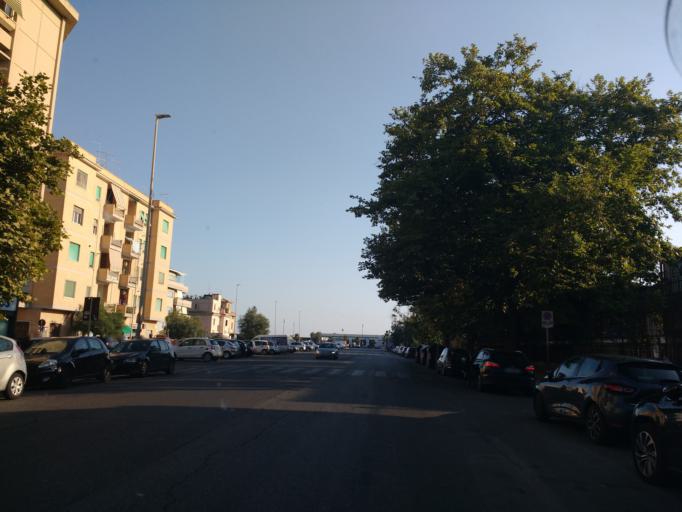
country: IT
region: Latium
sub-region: Citta metropolitana di Roma Capitale
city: Lido di Ostia
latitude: 41.7327
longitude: 12.2735
